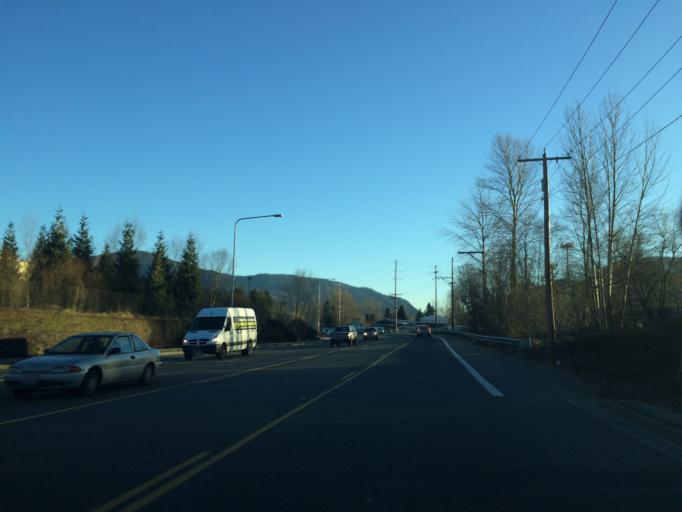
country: US
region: Washington
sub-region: King County
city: Issaquah
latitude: 47.5499
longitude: -122.0428
